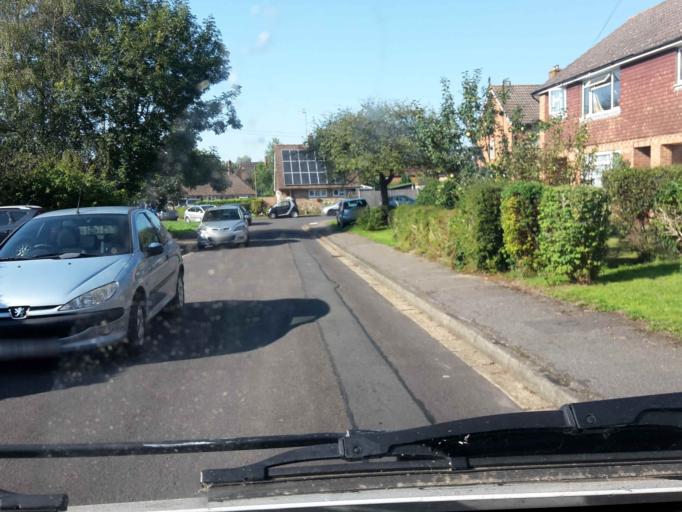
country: GB
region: England
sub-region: Surrey
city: Chilworth
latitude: 51.1821
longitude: -0.5269
